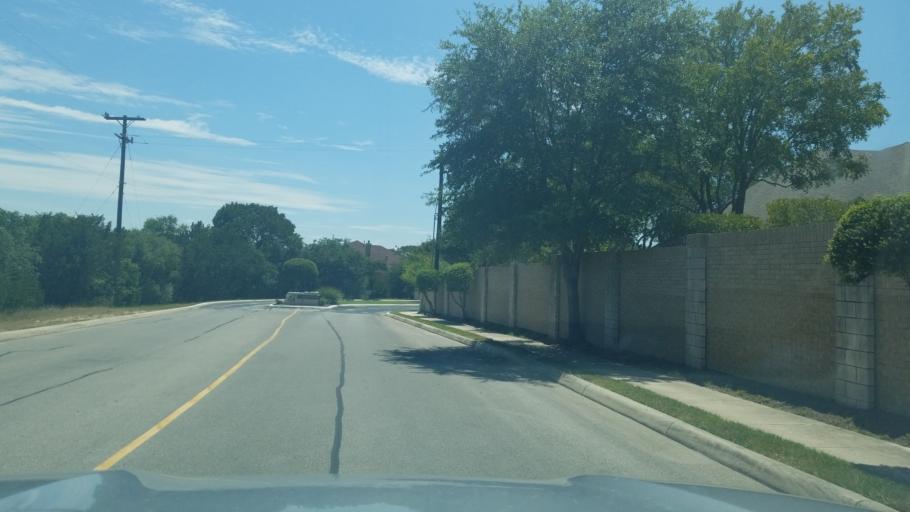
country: US
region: Texas
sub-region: Bexar County
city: Timberwood Park
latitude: 29.6587
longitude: -98.5080
